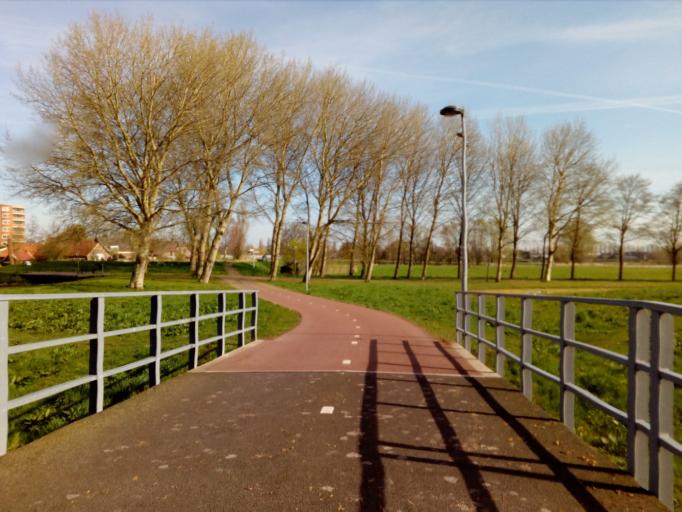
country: NL
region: South Holland
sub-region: Gemeente Schiedam
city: Schiedam
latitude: 51.9361
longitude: 4.3880
